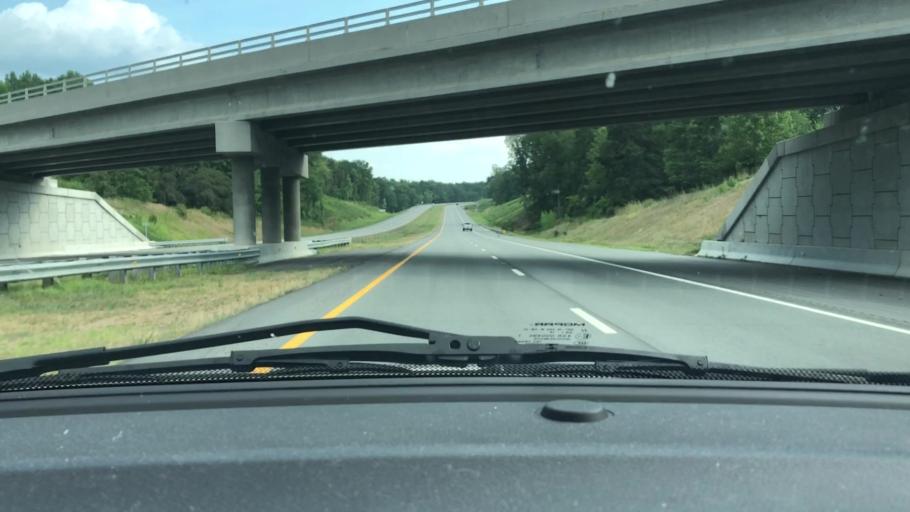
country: US
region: North Carolina
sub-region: Guilford County
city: Oak Ridge
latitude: 36.1528
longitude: -79.9594
